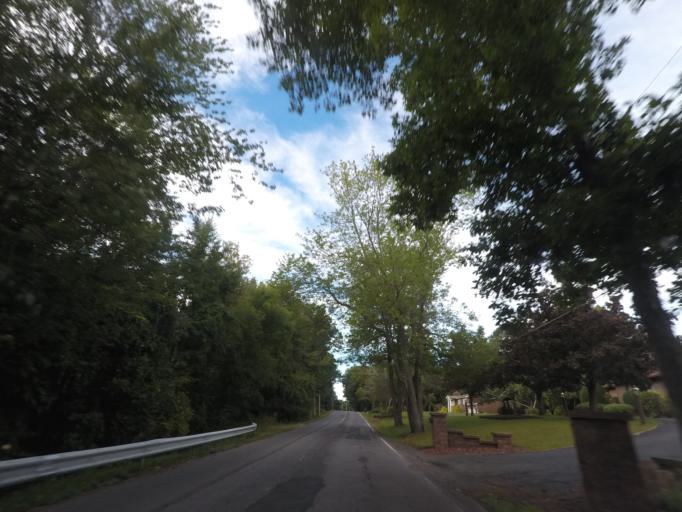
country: US
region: New York
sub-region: Rensselaer County
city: East Greenbush
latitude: 42.6055
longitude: -73.6763
